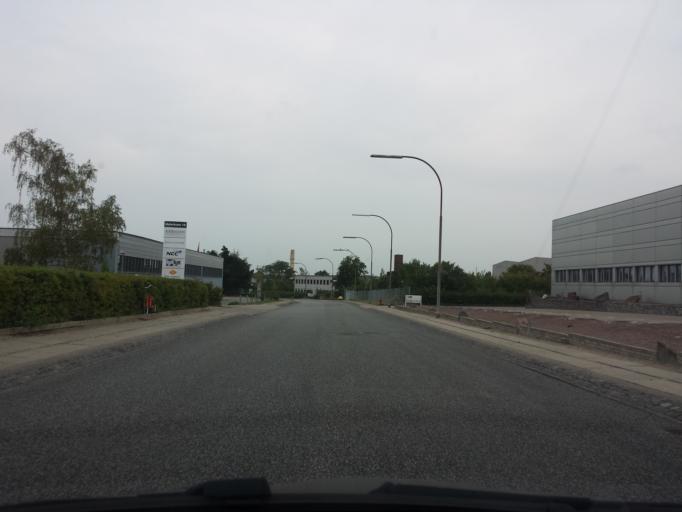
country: DK
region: Capital Region
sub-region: Herlev Kommune
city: Herlev
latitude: 55.7184
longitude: 12.4169
